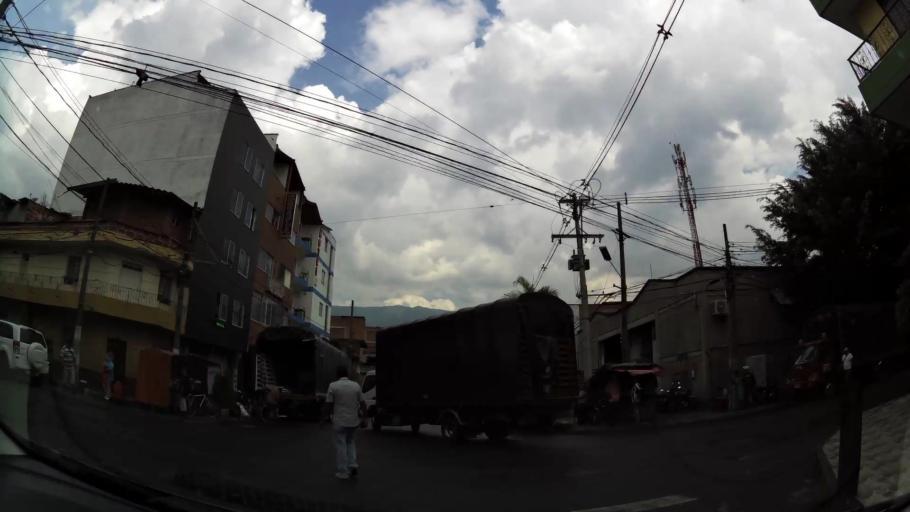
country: CO
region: Antioquia
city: Itagui
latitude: 6.1922
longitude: -75.5901
